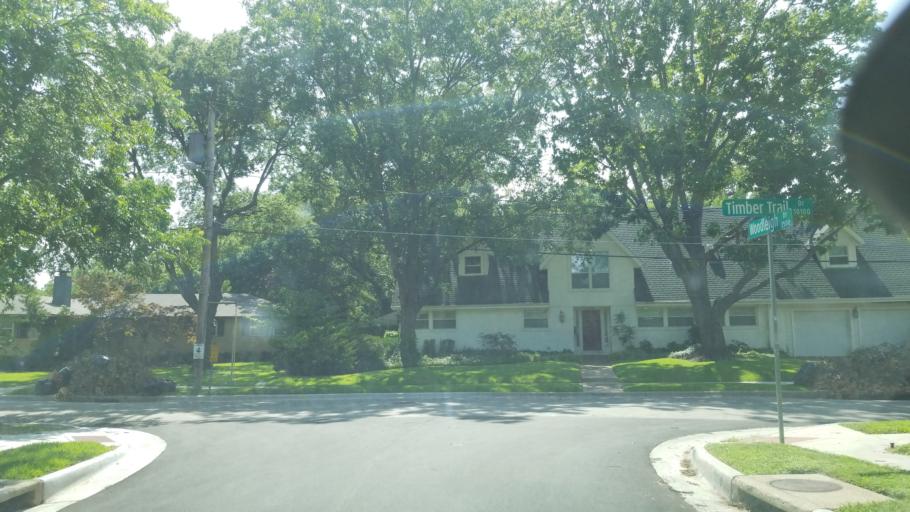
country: US
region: Texas
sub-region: Dallas County
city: Farmers Branch
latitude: 32.8838
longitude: -96.8607
